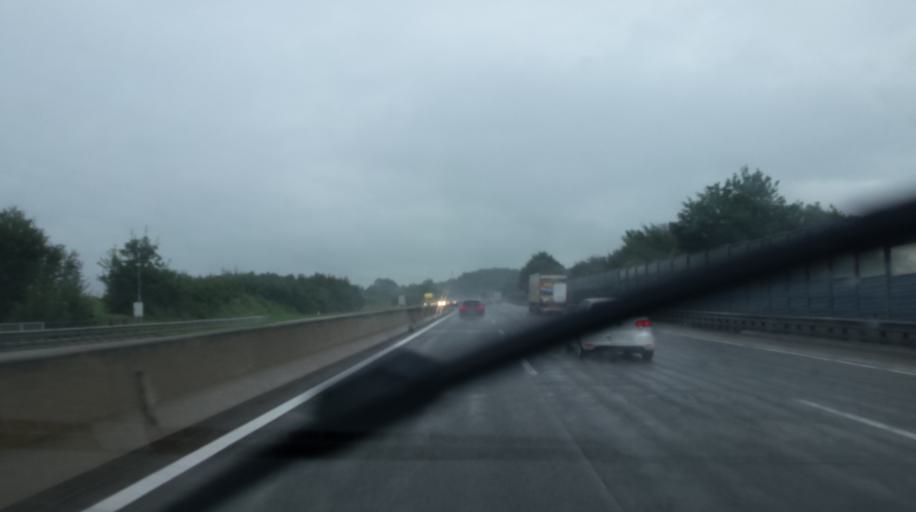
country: AT
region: Lower Austria
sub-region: Politischer Bezirk Amstetten
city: Sankt Valentin
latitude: 48.1734
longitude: 14.5477
